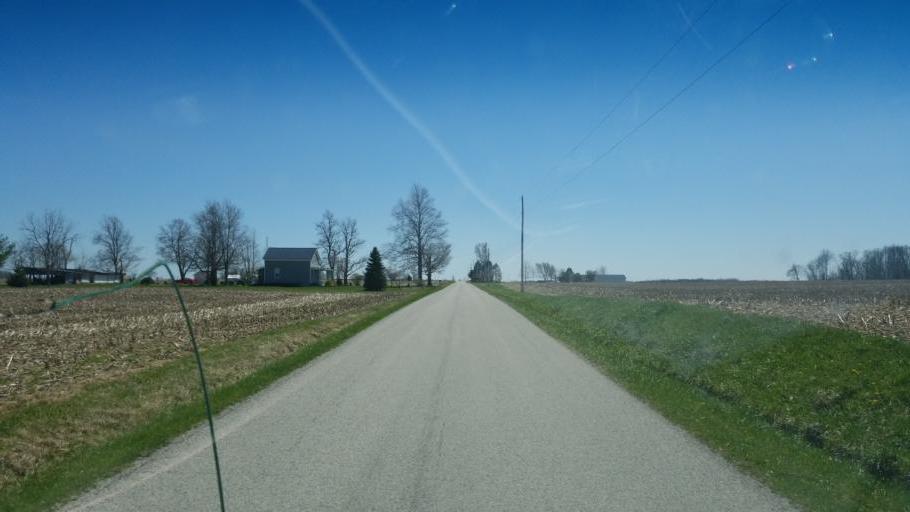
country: US
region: Ohio
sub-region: Huron County
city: Willard
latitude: 41.0622
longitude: -82.8424
